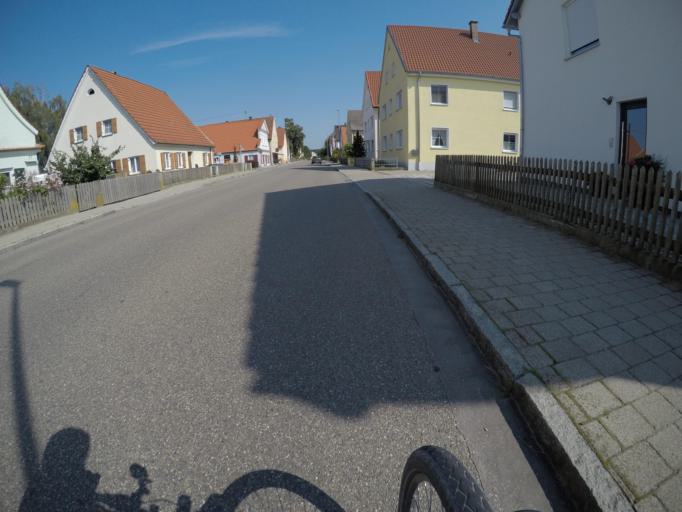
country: DE
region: Bavaria
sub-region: Swabia
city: Binswangen
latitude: 48.5591
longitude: 10.6435
